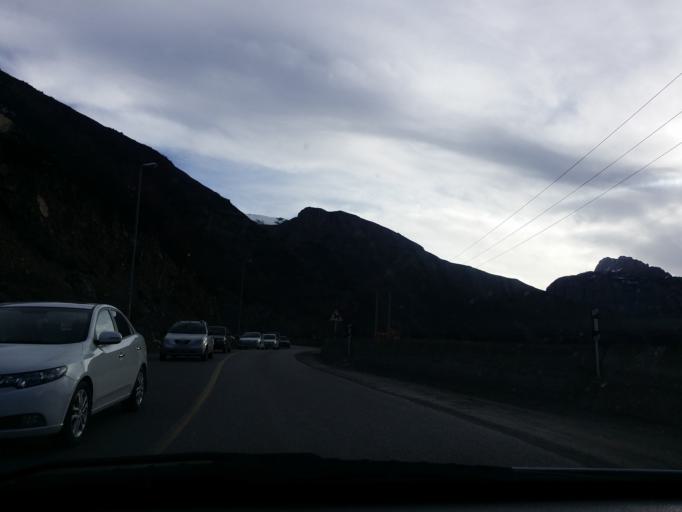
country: IR
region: Mazandaran
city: Chalus
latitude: 36.2504
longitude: 51.2842
